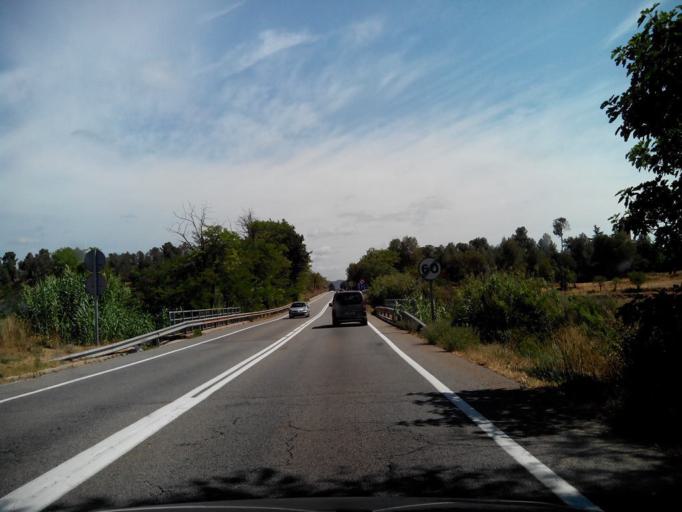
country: ES
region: Catalonia
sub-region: Provincia de Barcelona
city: Sant Fruitos de Bages
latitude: 41.7532
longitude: 1.8648
